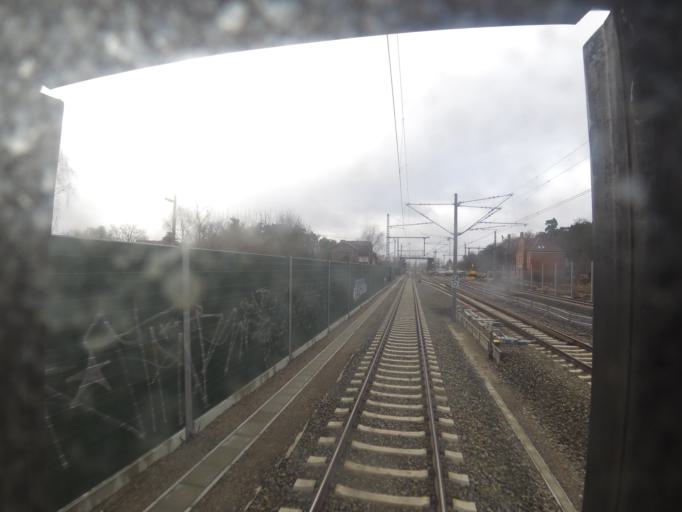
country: DE
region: Brandenburg
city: Rangsdorf
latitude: 52.2972
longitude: 13.4299
